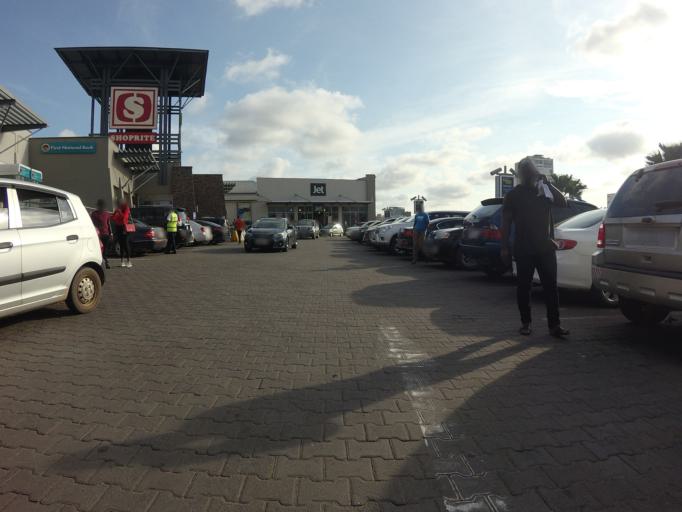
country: GH
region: Greater Accra
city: Medina Estates
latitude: 5.6223
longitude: -0.1738
